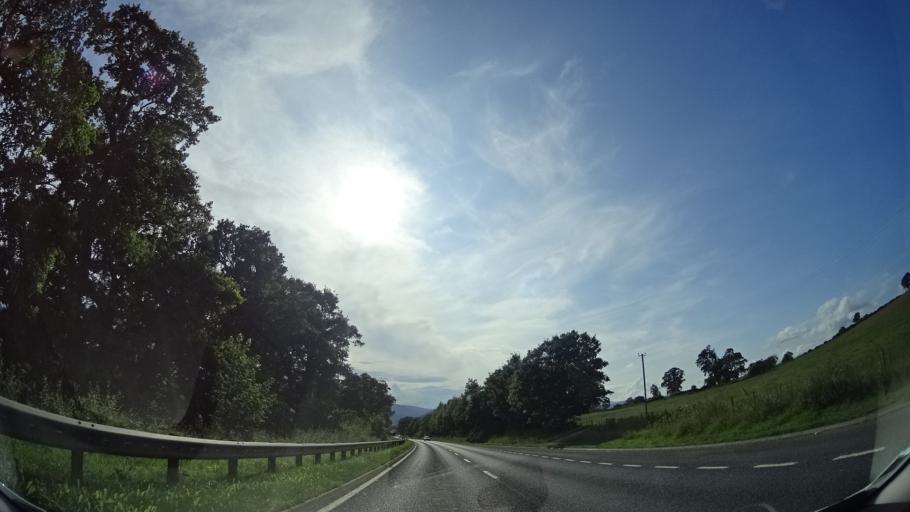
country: GB
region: Scotland
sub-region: Highland
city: Muir of Ord
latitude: 57.5588
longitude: -4.5293
